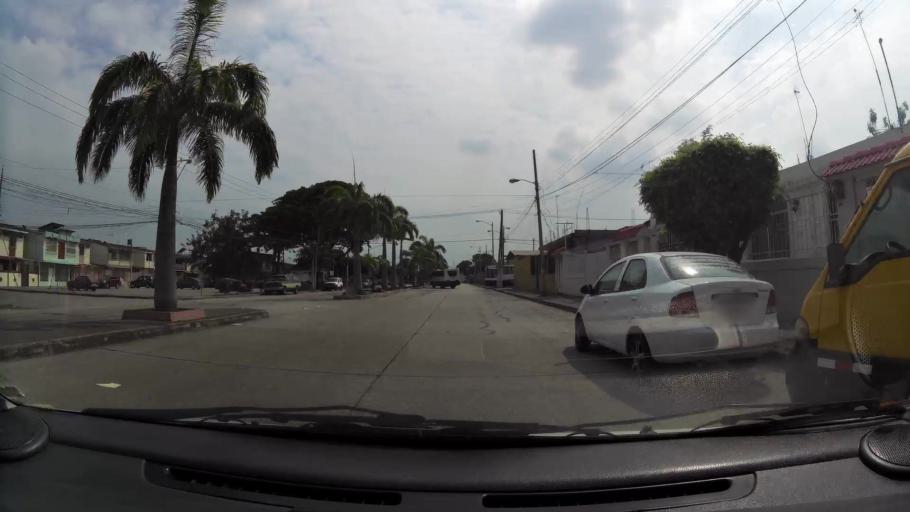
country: EC
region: Guayas
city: Guayaquil
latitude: -2.2411
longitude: -79.9022
